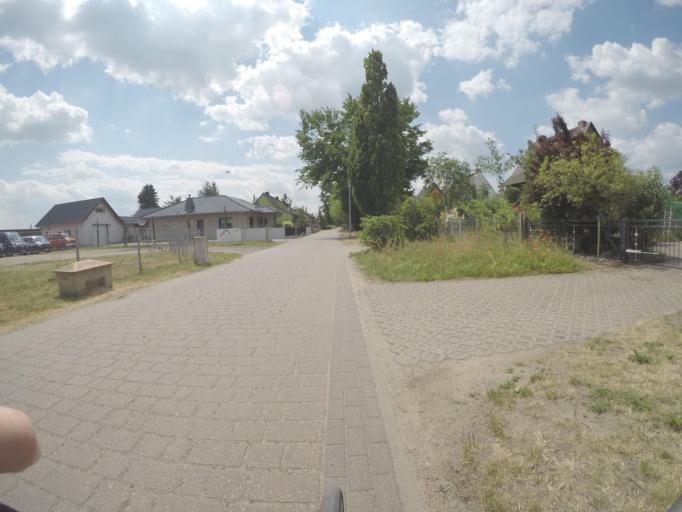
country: DE
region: Brandenburg
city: Roskow
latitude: 52.4592
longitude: 12.6802
